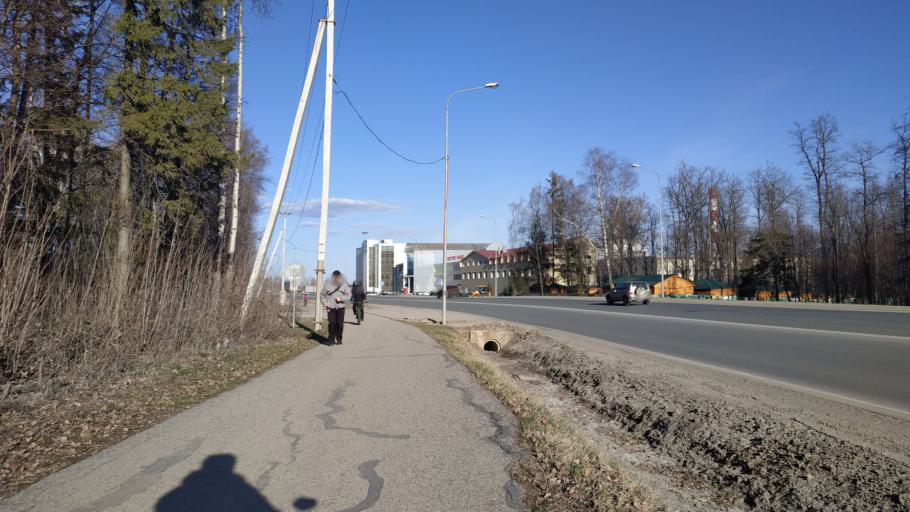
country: RU
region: Chuvashia
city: Novyye Lapsary
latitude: 56.1297
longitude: 47.1593
